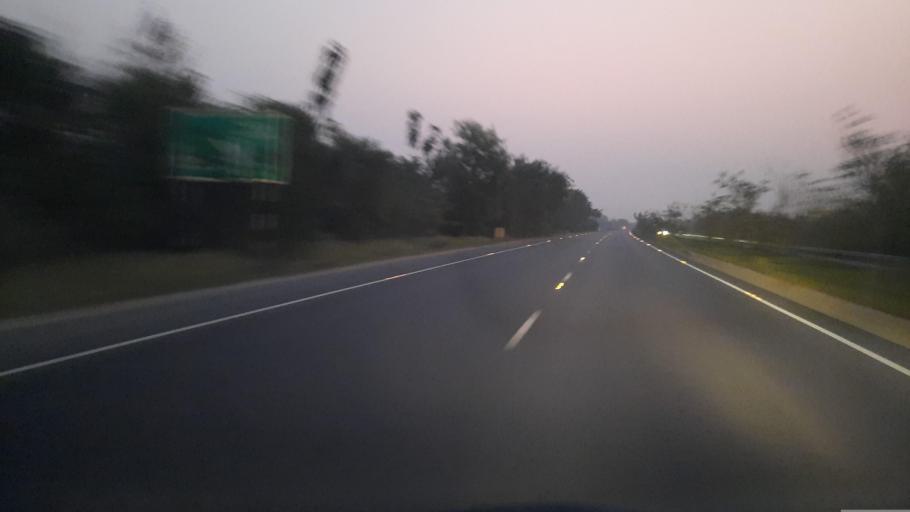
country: BD
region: Dhaka
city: Char Bhadrasan
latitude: 23.4000
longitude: 90.2105
